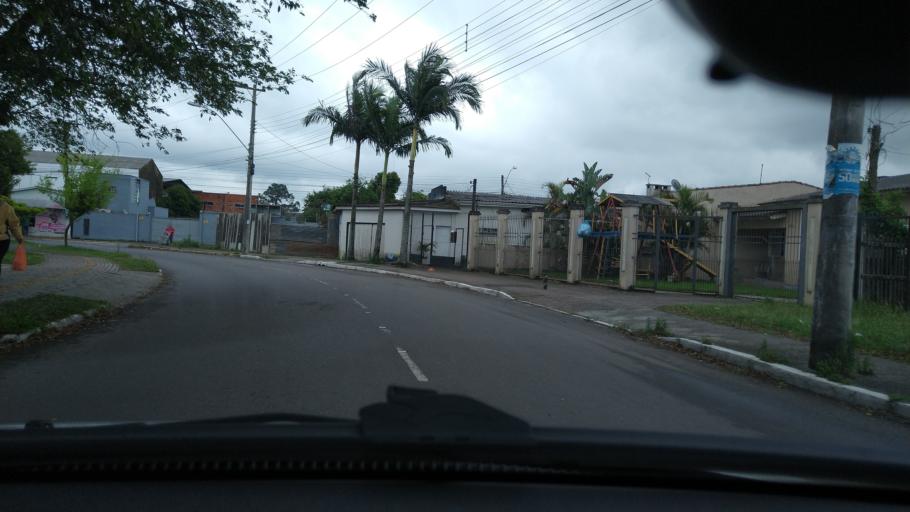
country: BR
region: Rio Grande do Sul
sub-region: Canoas
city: Canoas
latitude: -29.9007
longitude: -51.2184
